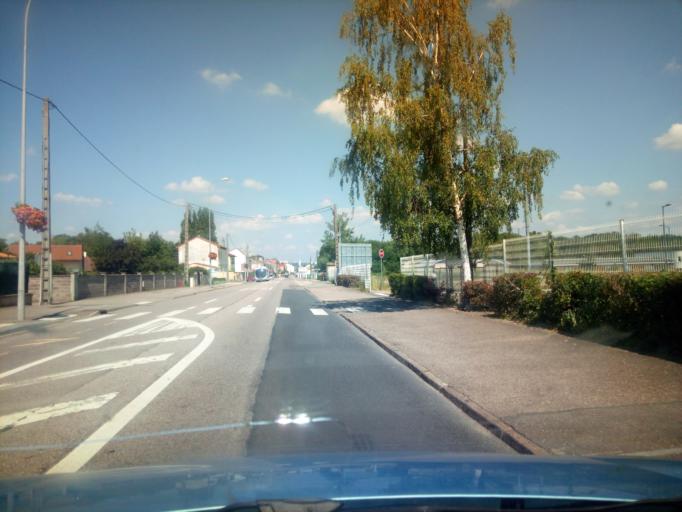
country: FR
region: Lorraine
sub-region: Departement de Meurthe-et-Moselle
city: Laneuveville-devant-Nancy
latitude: 48.6615
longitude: 6.2224
